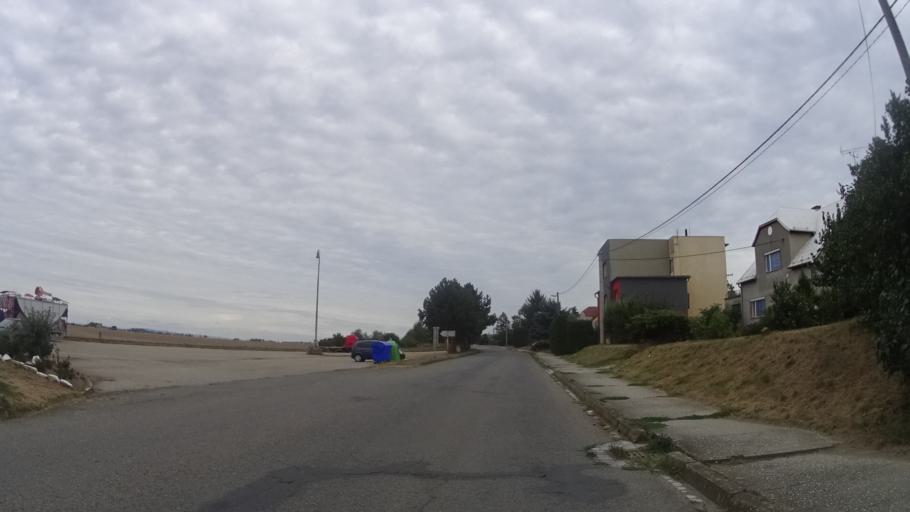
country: CZ
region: Olomoucky
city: Tovacov
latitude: 49.3999
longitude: 17.2881
